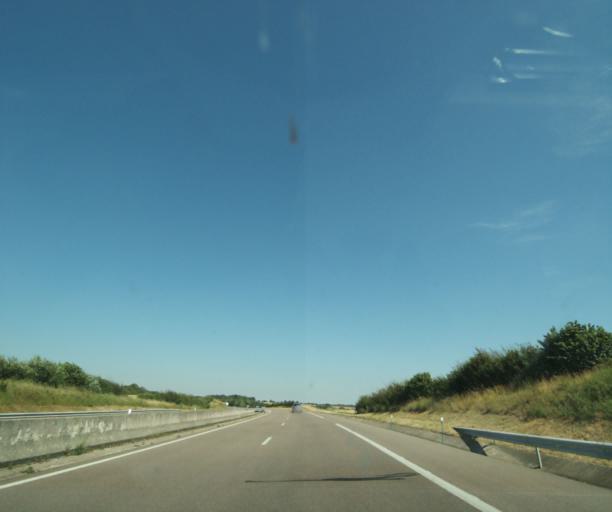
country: FR
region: Lorraine
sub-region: Departement des Vosges
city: Chatenois
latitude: 48.4031
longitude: 5.8792
